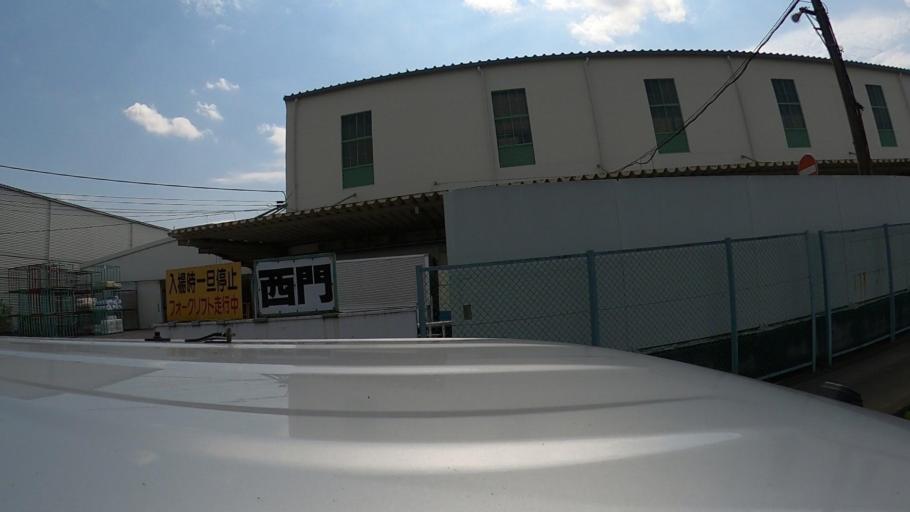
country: JP
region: Kanagawa
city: Chigasaki
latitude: 35.3606
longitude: 139.3730
